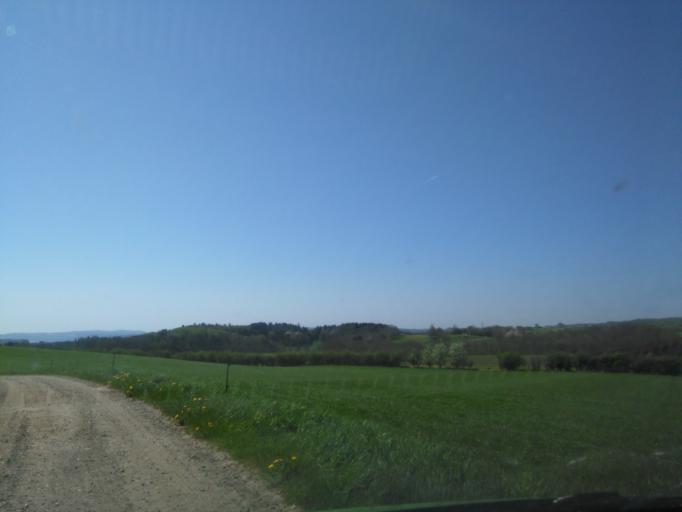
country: DK
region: Central Jutland
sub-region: Odder Kommune
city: Odder
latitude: 55.9000
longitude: 10.0353
